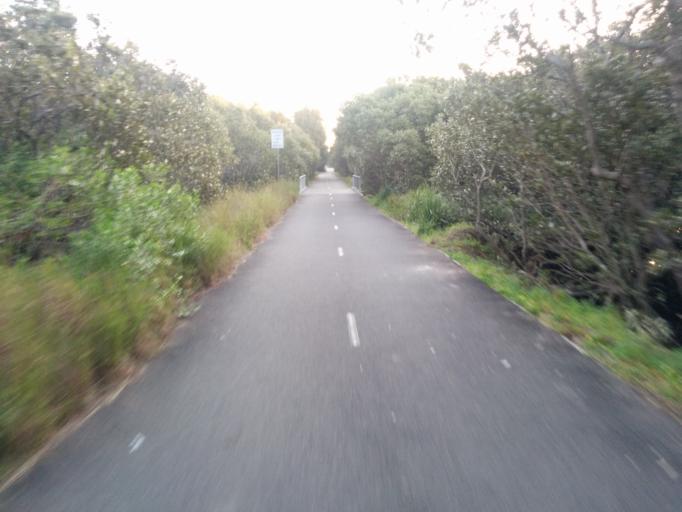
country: AU
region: New South Wales
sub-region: Canada Bay
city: Concord West
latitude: -33.8440
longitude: 151.0822
